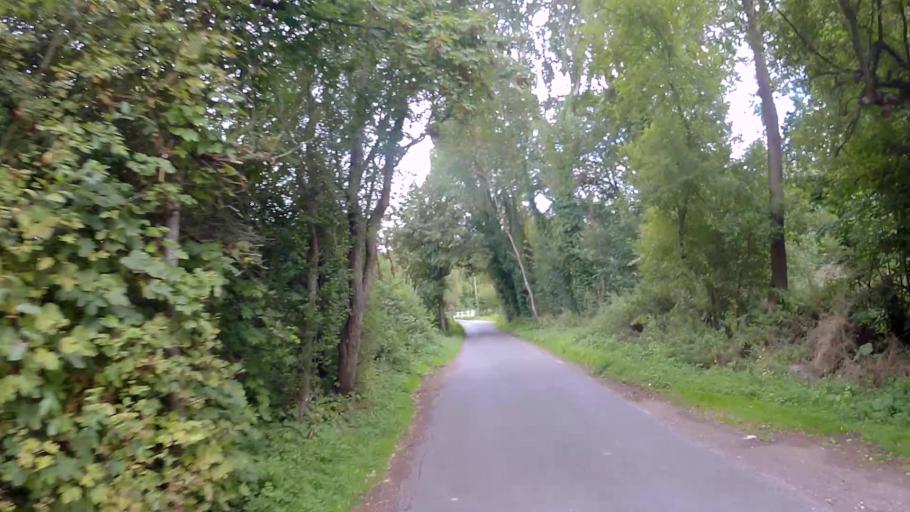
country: GB
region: England
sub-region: Hampshire
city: Kings Worthy
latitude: 51.1680
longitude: -1.3389
